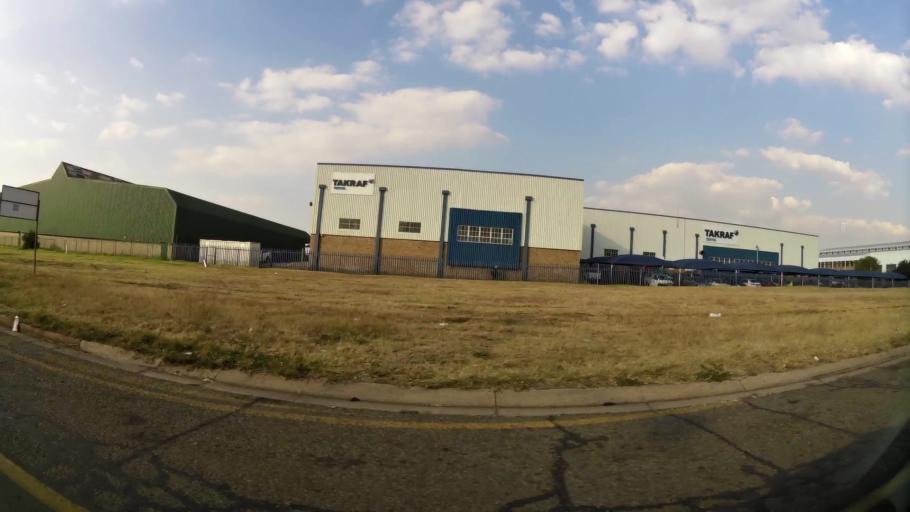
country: ZA
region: Gauteng
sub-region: City of Johannesburg Metropolitan Municipality
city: Modderfontein
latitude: -26.1226
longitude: 28.2010
